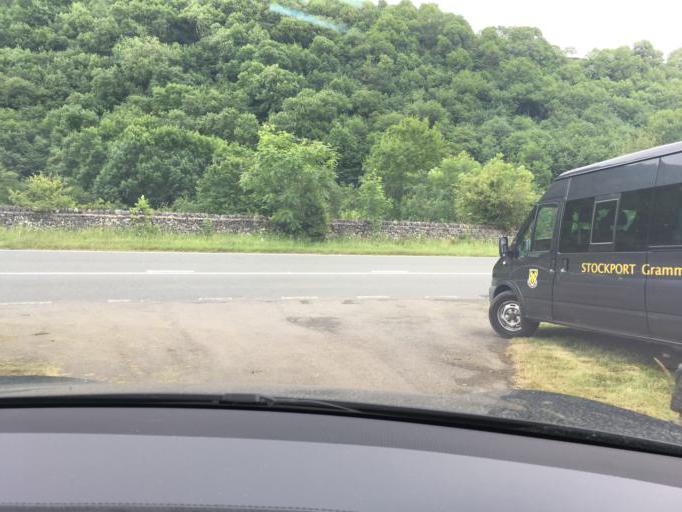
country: GB
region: England
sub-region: Derbyshire
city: Tideswell
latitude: 53.2314
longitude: -1.7453
